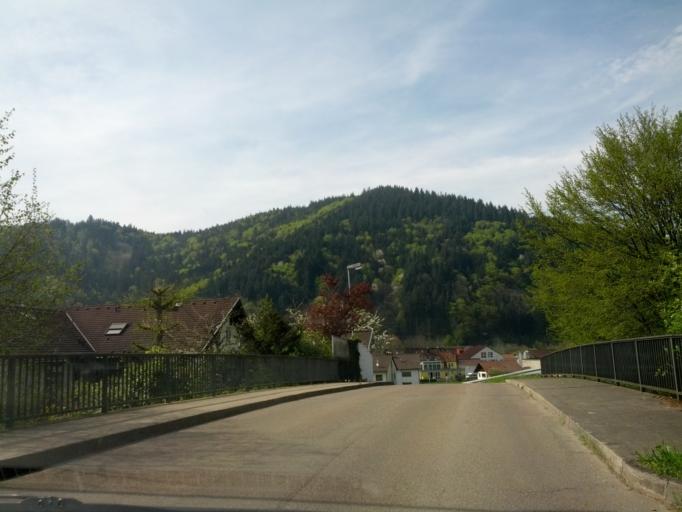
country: DE
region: Baden-Wuerttemberg
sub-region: Freiburg Region
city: Gutach im Breisgau
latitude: 48.1165
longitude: 7.9956
